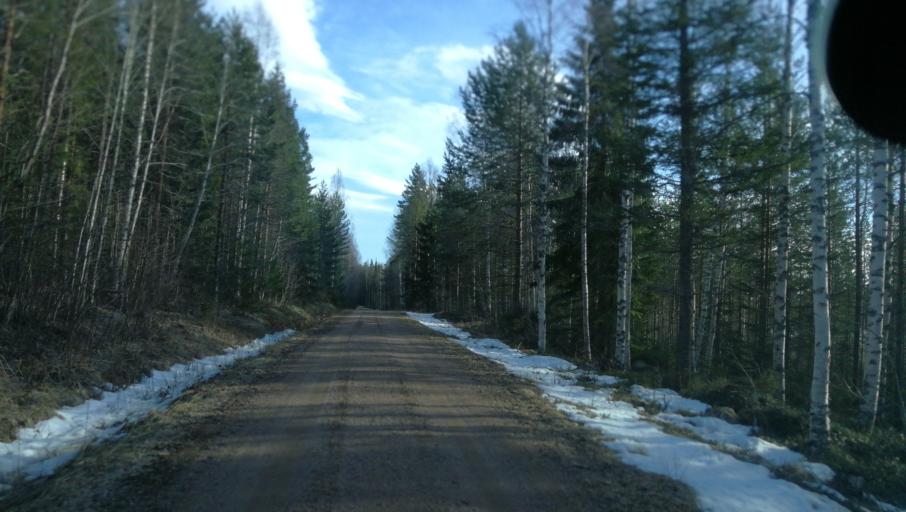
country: SE
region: Dalarna
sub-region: Vansbro Kommun
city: Vansbro
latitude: 60.8056
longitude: 14.2084
